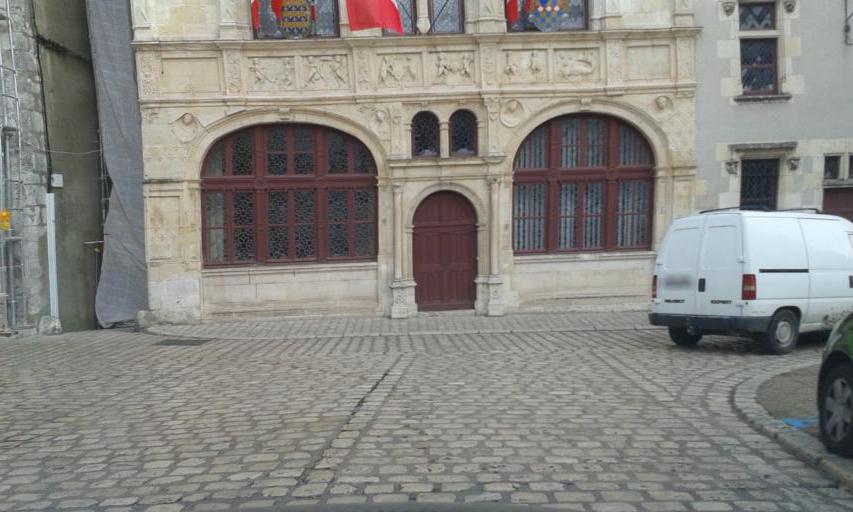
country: FR
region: Centre
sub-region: Departement du Loiret
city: Beaugency
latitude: 47.7779
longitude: 1.6313
